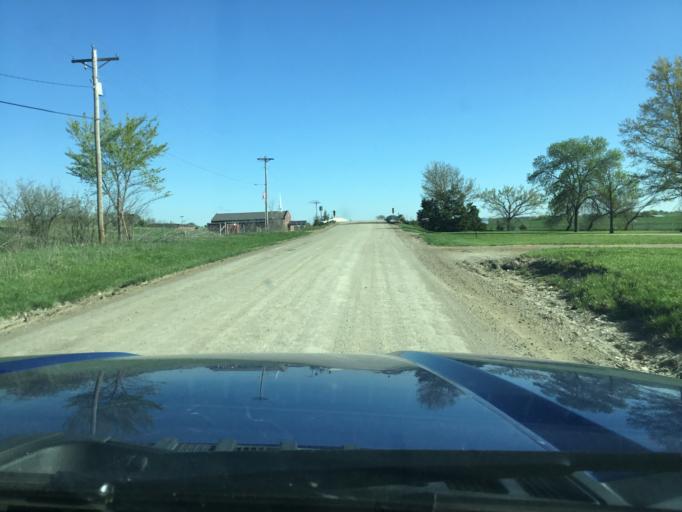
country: US
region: Kansas
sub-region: Douglas County
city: Lawrence
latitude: 38.9958
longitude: -95.3539
